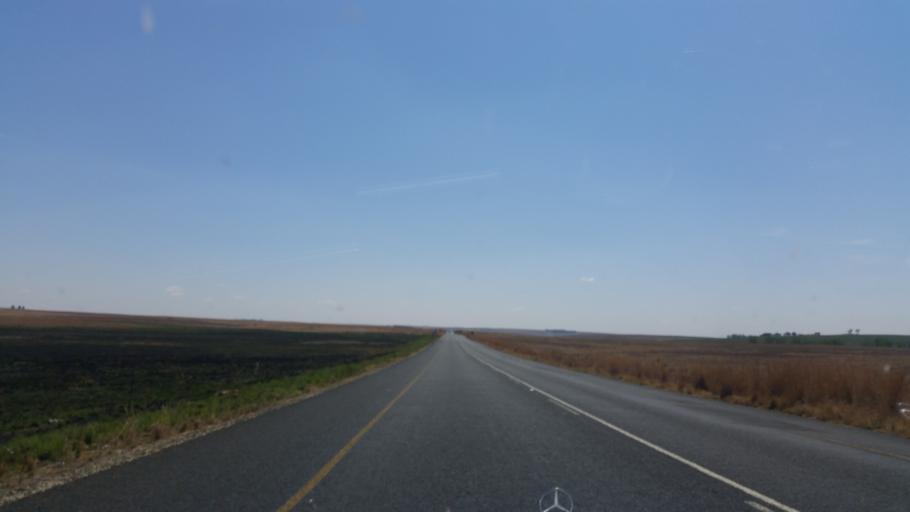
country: ZA
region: Orange Free State
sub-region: Thabo Mofutsanyana District Municipality
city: Bethlehem
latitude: -28.1661
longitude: 28.6833
